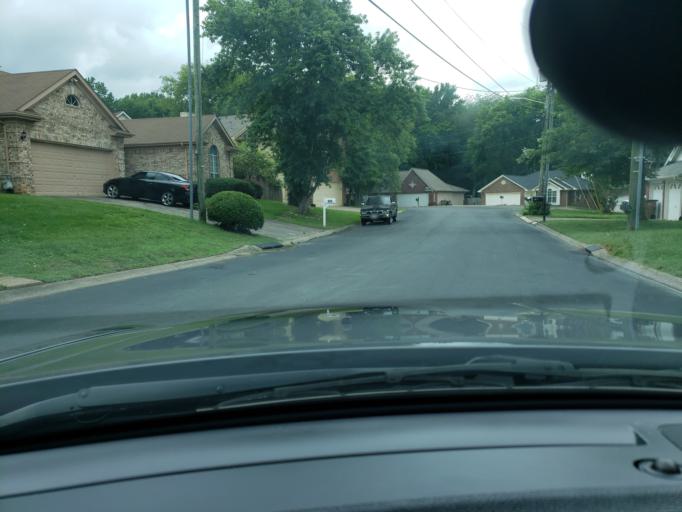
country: US
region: Tennessee
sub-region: Williamson County
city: Nolensville
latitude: 36.0359
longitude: -86.6783
